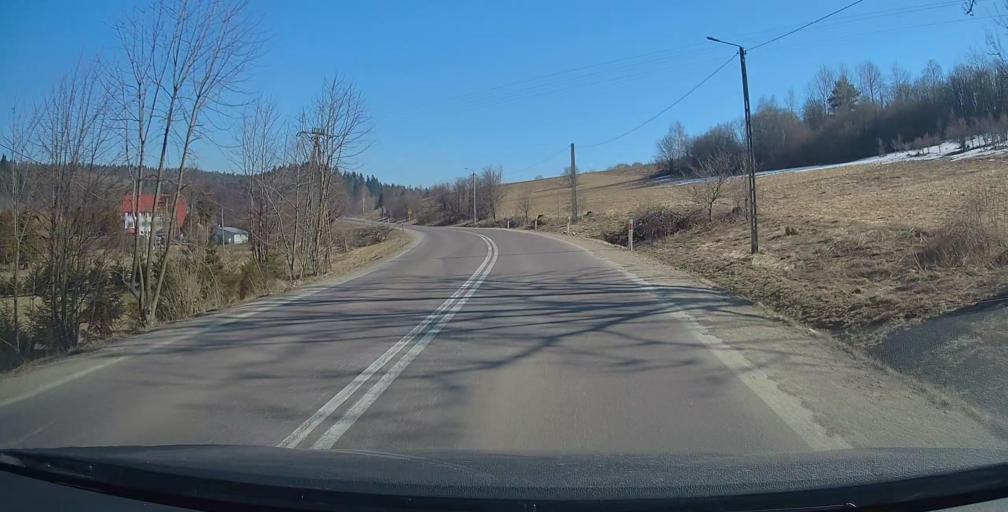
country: PL
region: Subcarpathian Voivodeship
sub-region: Powiat bieszczadzki
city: Ustrzyki Dolne
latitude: 49.5543
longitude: 22.5639
